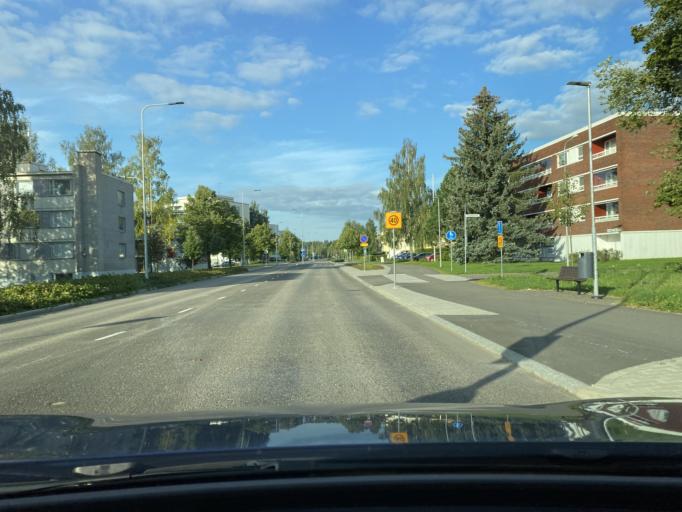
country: FI
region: Kymenlaakso
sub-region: Kouvola
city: Kouvola
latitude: 60.9061
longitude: 26.6180
